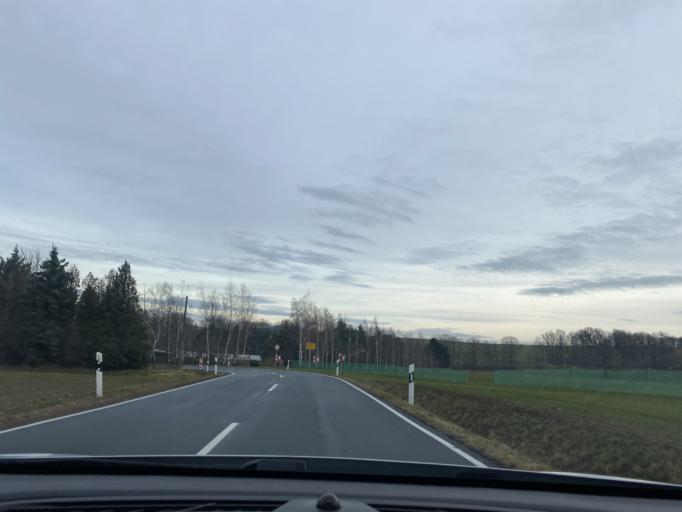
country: DE
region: Saxony
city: Markersdorf
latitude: 51.1107
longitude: 14.8475
